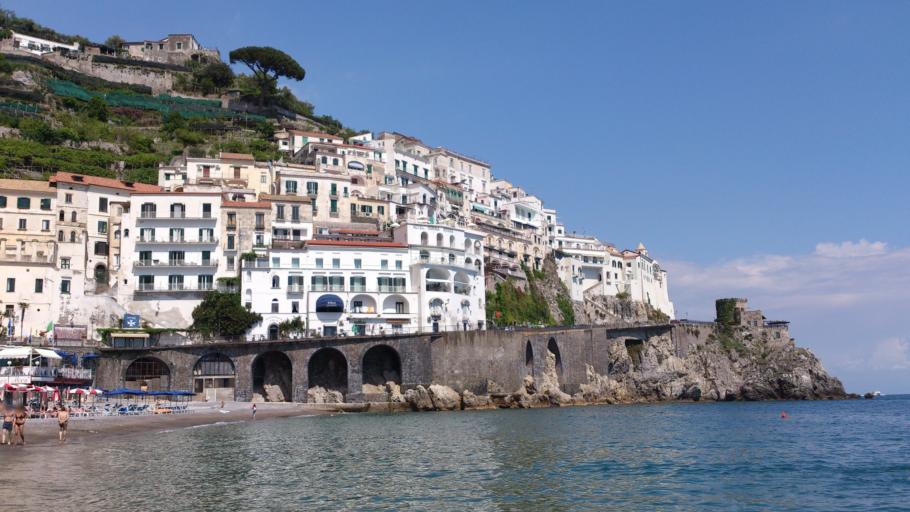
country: IT
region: Campania
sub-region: Provincia di Salerno
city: Amalfi
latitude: 40.6334
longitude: 14.6031
